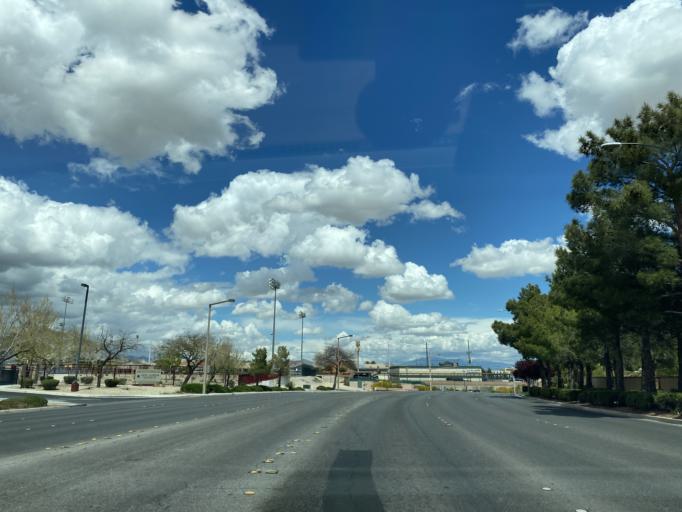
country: US
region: Nevada
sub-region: Clark County
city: Summerlin South
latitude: 36.1540
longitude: -115.3158
